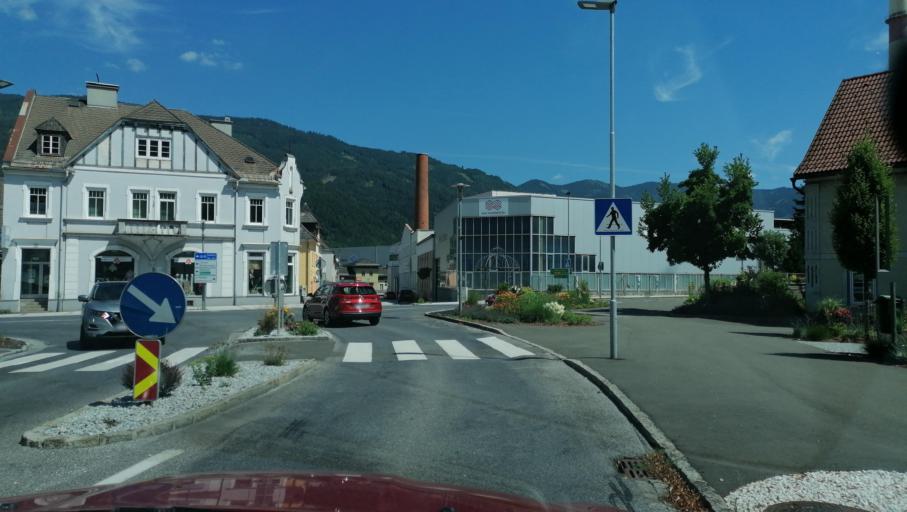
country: AT
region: Styria
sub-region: Politischer Bezirk Liezen
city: Trieben
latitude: 47.4876
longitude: 14.4874
